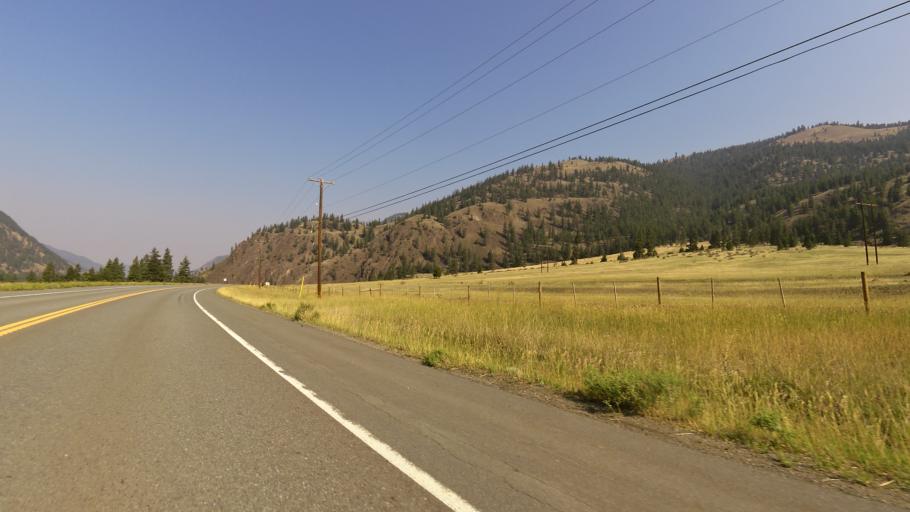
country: CA
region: British Columbia
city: Princeton
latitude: 49.3555
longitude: -120.0938
